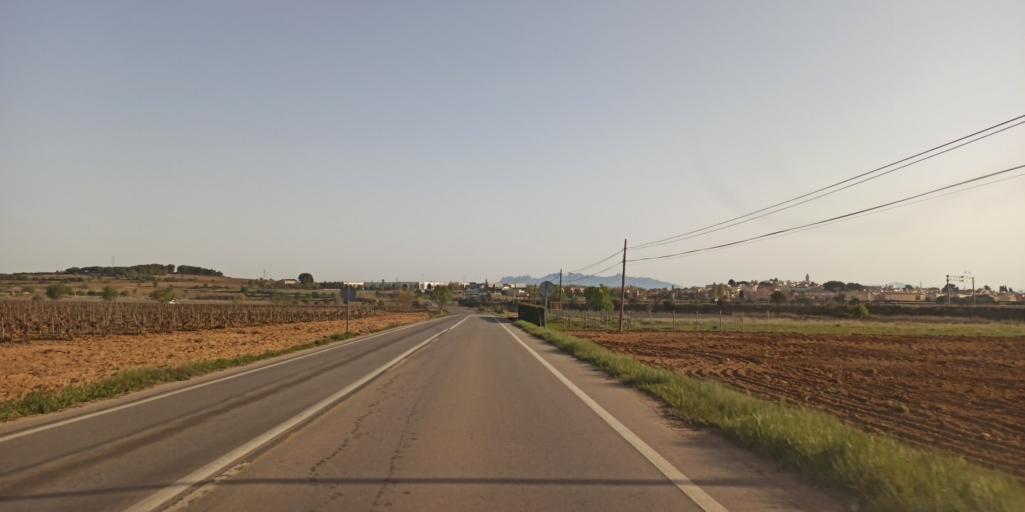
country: ES
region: Catalonia
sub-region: Provincia de Barcelona
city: La Granada
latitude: 41.3680
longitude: 1.7101
